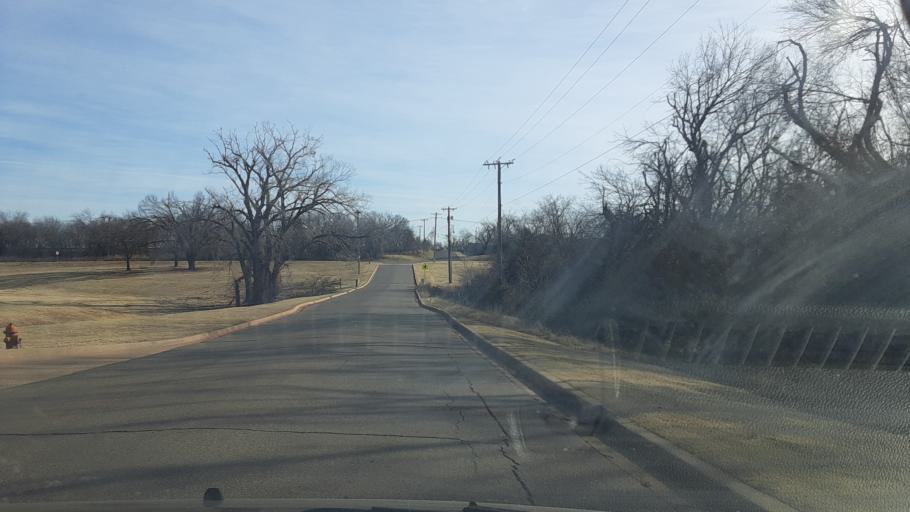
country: US
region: Oklahoma
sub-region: Logan County
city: Guthrie
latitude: 35.8926
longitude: -97.4183
